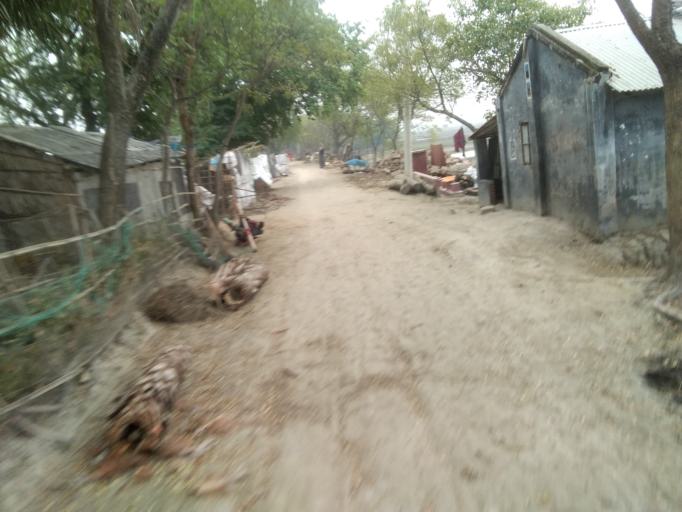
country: BD
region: Khulna
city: Satkhira
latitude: 22.5712
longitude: 89.0778
